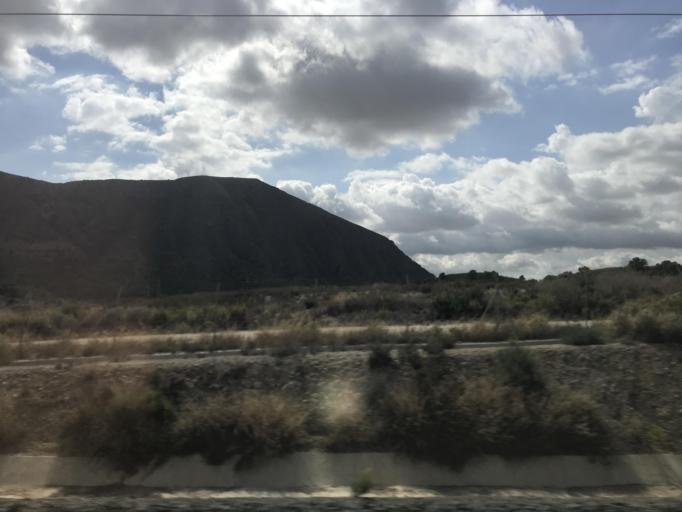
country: ES
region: Valencia
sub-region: Provincia de Alicante
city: San Vicent del Raspeig
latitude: 38.3652
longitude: -0.5946
